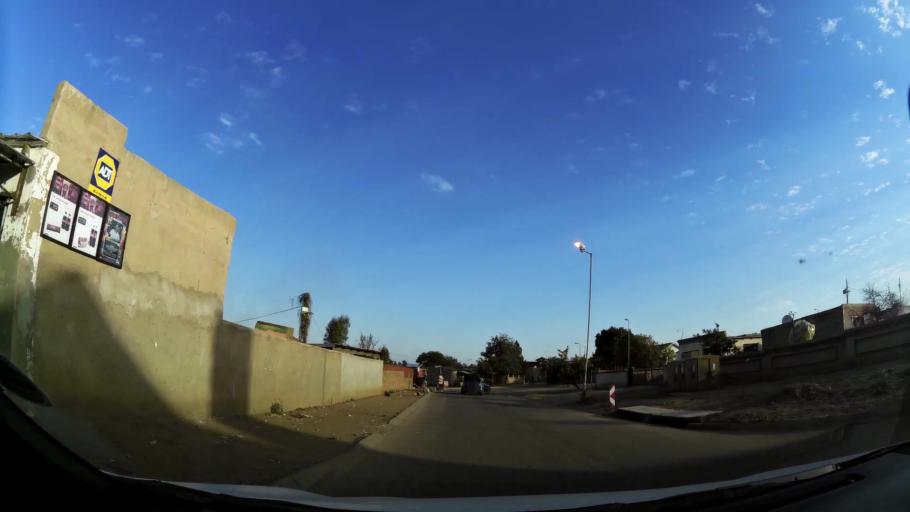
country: ZA
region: Gauteng
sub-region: City of Tshwane Metropolitan Municipality
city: Cullinan
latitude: -25.7130
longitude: 28.3647
